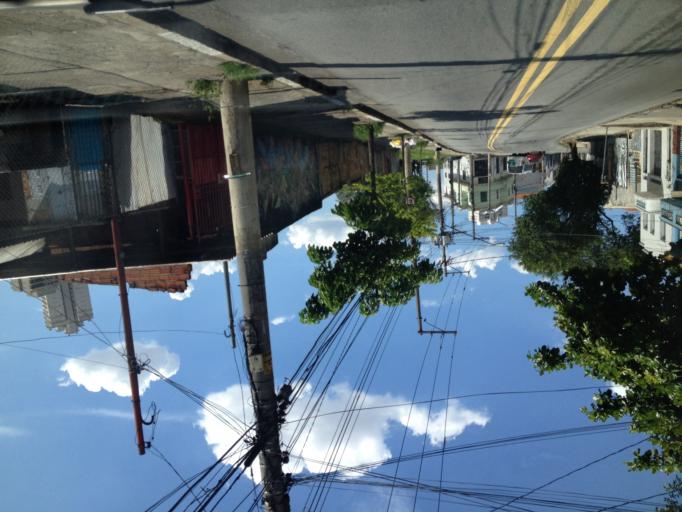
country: BR
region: Sao Paulo
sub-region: Sao Paulo
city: Sao Paulo
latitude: -23.5586
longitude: -46.5771
